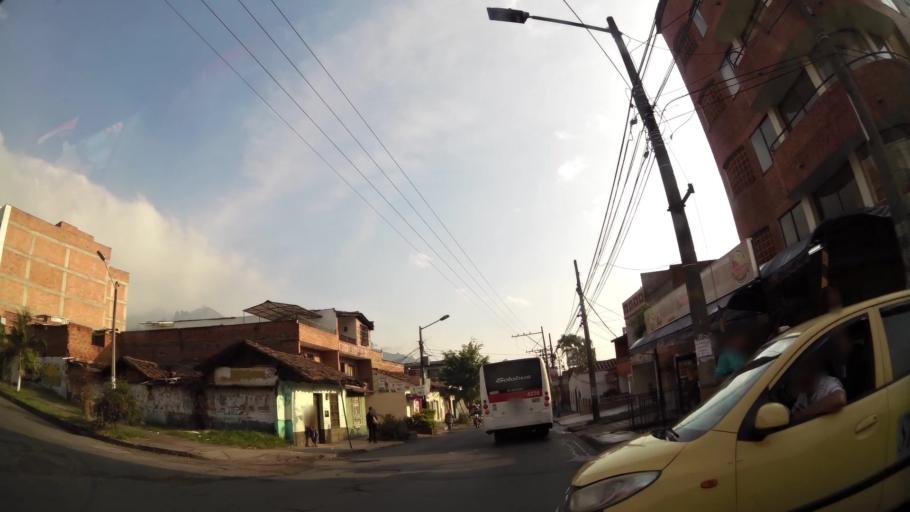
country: CO
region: Antioquia
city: Sabaneta
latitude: 6.1662
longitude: -75.6209
